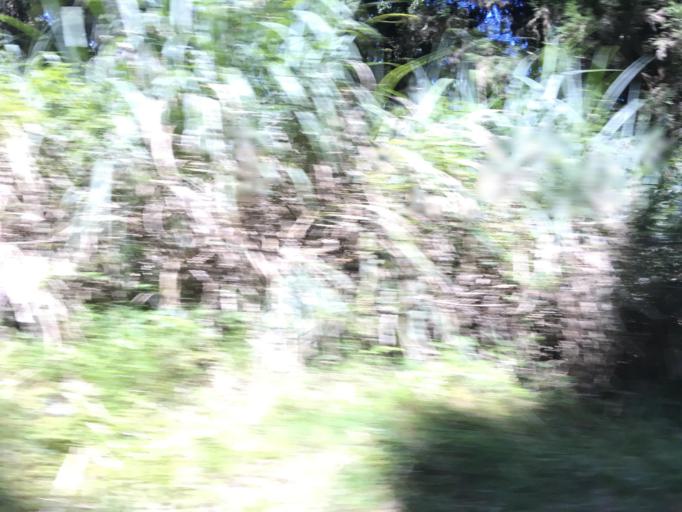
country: TW
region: Taiwan
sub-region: Yilan
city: Yilan
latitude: 24.5209
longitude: 121.5190
